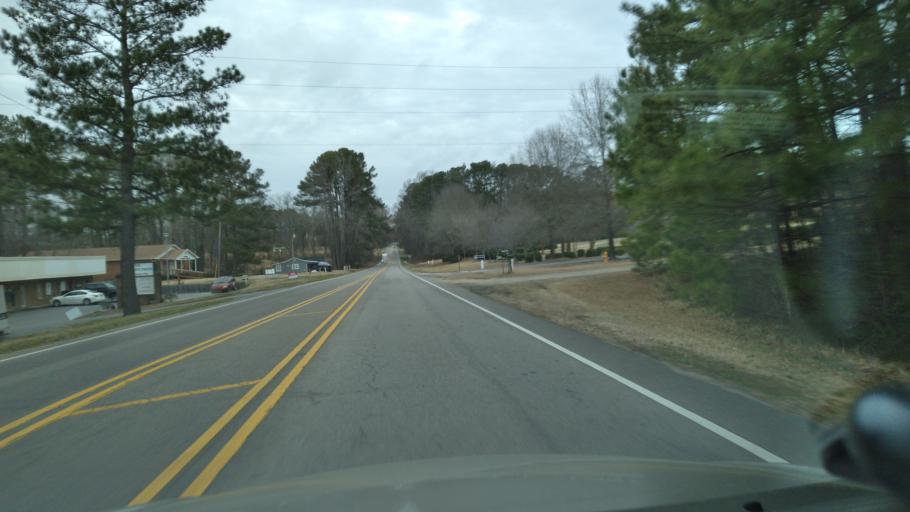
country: US
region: North Carolina
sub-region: Wake County
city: Garner
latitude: 35.6934
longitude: -78.6075
